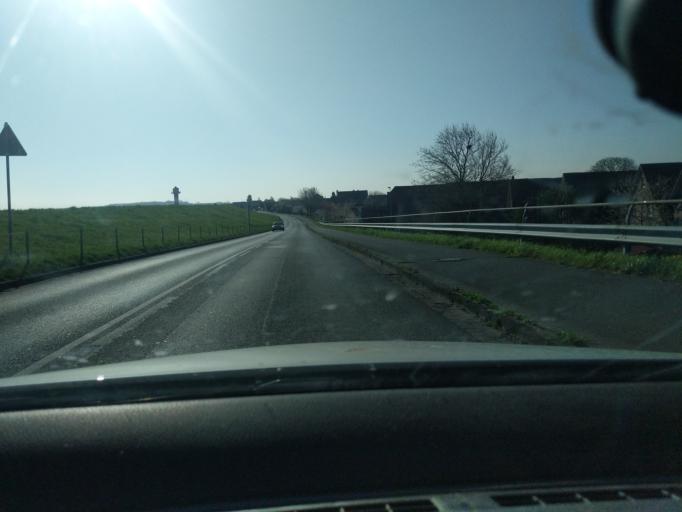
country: DE
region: Lower Saxony
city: Grunendeich
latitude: 53.5710
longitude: 9.6343
